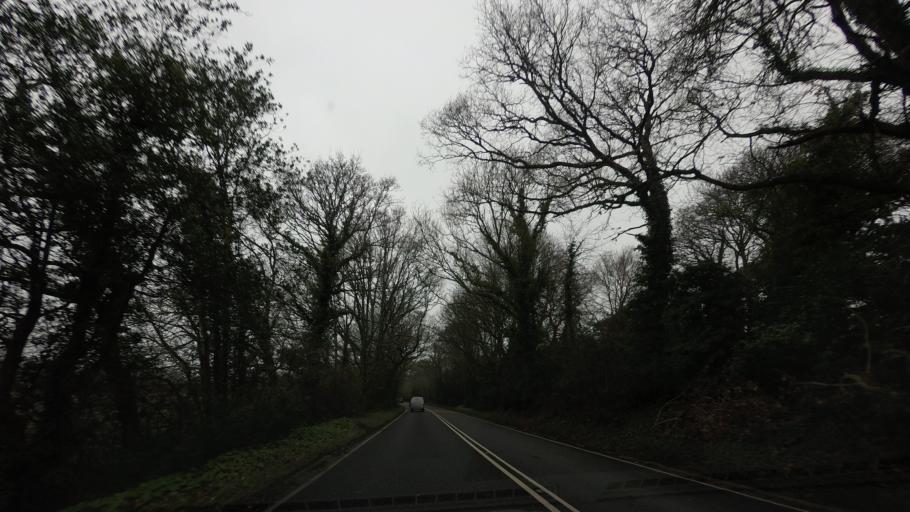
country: GB
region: England
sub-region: East Sussex
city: Battle
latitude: 50.9430
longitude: 0.5122
